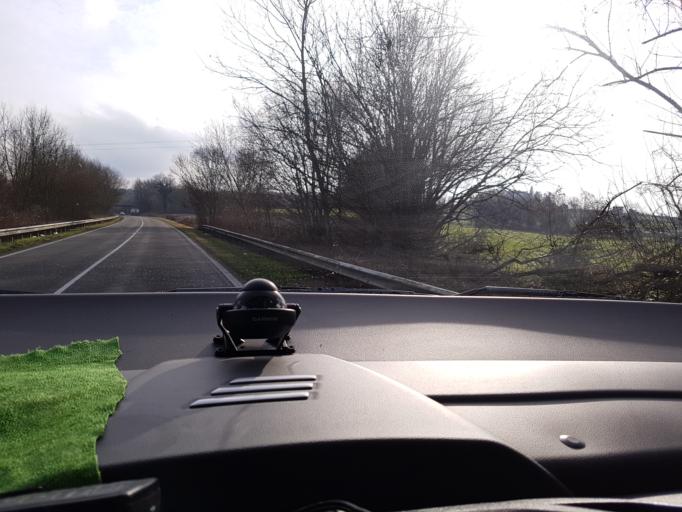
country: FR
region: Nord-Pas-de-Calais
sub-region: Departement du Nord
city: Fourmies
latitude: 50.0142
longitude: 4.0303
